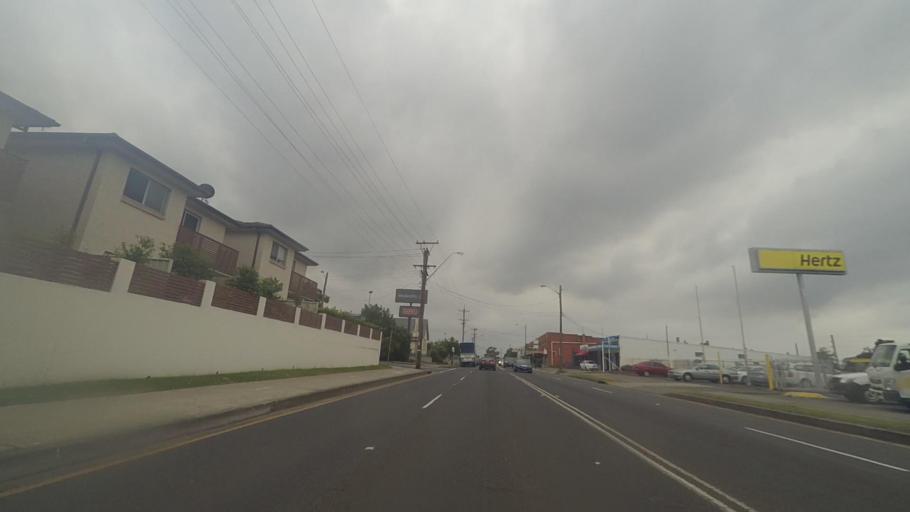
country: AU
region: New South Wales
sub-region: Wollongong
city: Cordeaux Heights
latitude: -34.4564
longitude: 150.8433
